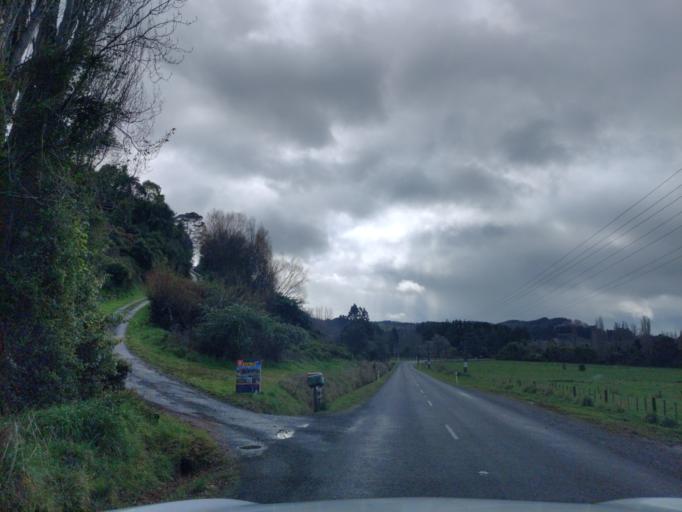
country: NZ
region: Manawatu-Wanganui
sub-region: Palmerston North City
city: Palmerston North
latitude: -40.1793
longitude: 175.7890
